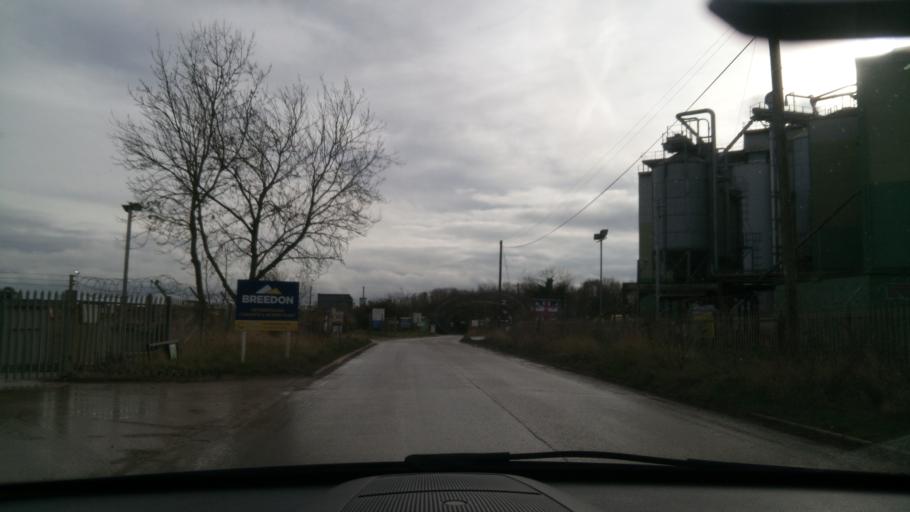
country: GB
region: England
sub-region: Peterborough
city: Eye
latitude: 52.6034
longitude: -0.2244
